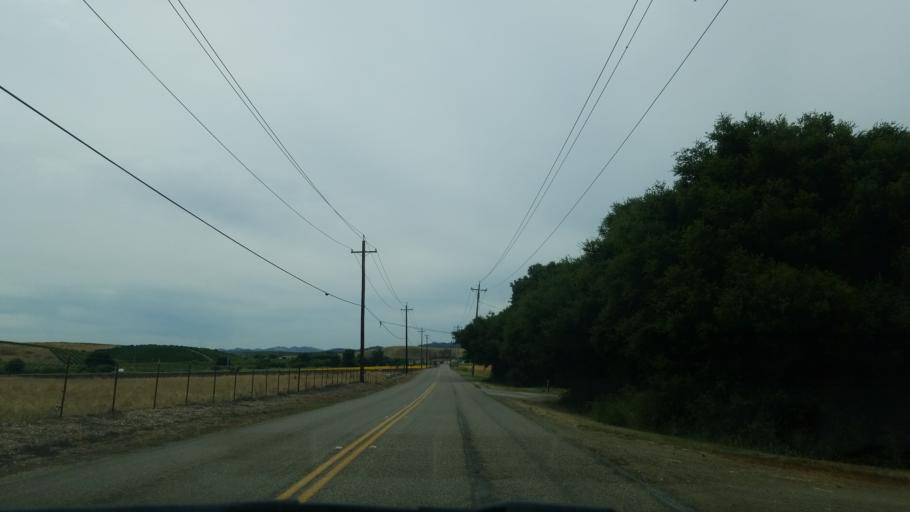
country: US
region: California
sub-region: San Luis Obispo County
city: San Luis Obispo
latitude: 35.2232
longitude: -120.5982
